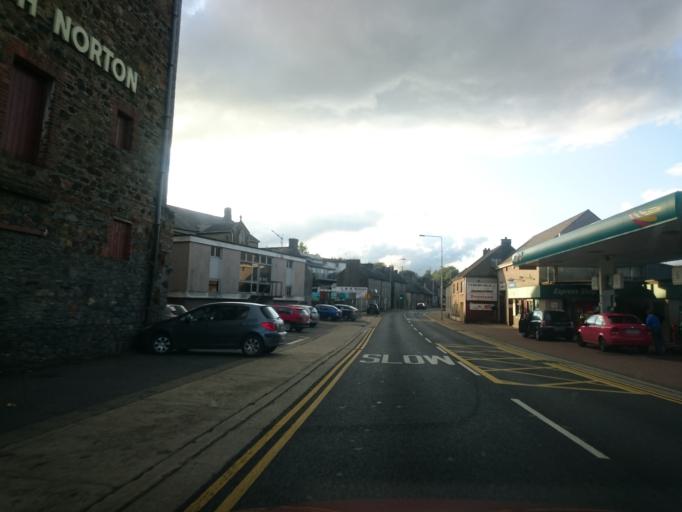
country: IE
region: Leinster
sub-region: Loch Garman
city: Enniscorthy
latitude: 52.5034
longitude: -6.5687
